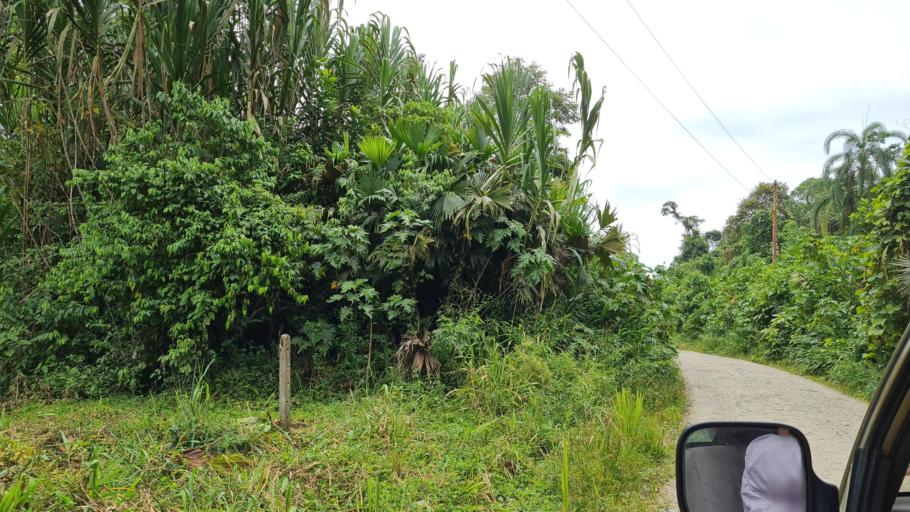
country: EC
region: Napo
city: Tena
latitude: -0.9994
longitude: -77.7585
